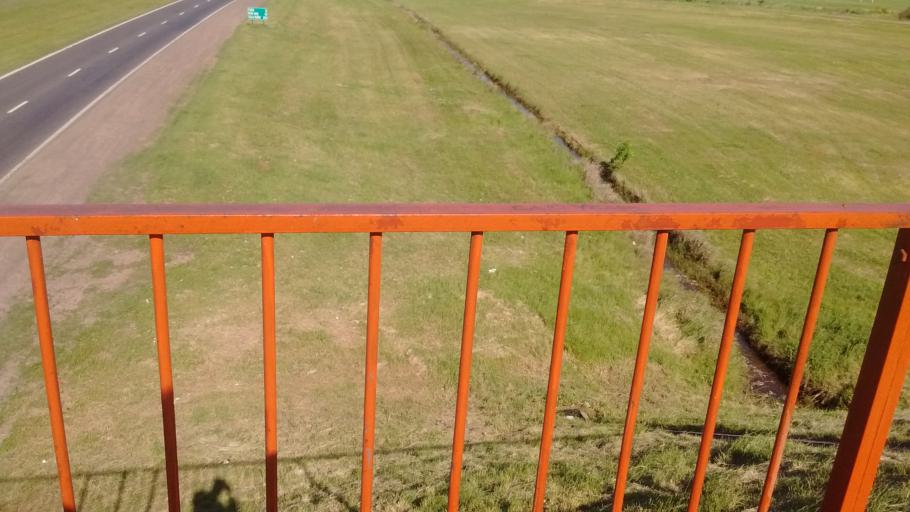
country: AR
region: Santa Fe
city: Perez
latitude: -32.9494
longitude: -60.7381
